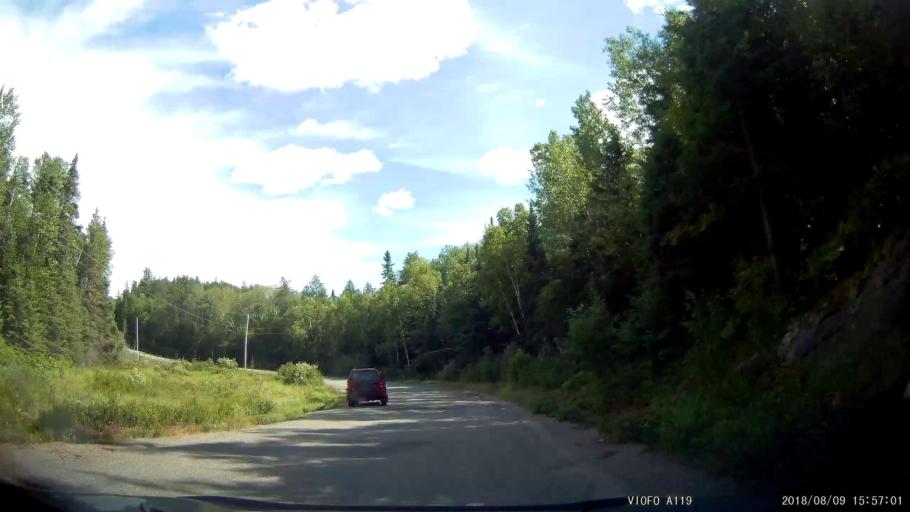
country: CA
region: Ontario
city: Rayside-Balfour
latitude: 46.6084
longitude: -81.5095
